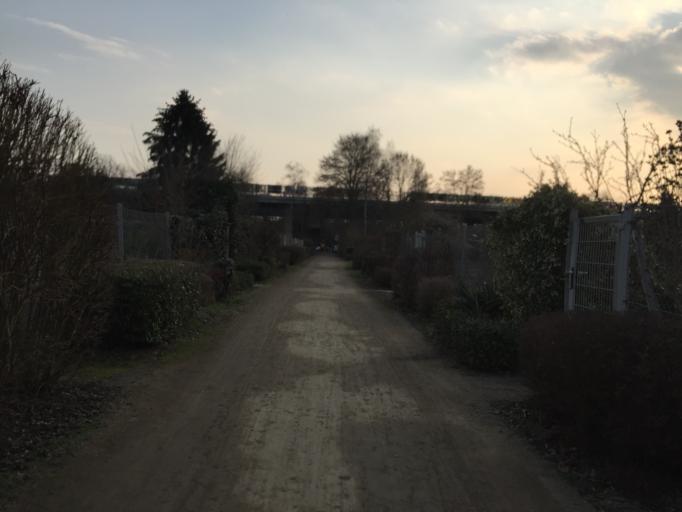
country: DE
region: Hesse
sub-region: Regierungsbezirk Darmstadt
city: Frankfurt am Main
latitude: 50.1346
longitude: 8.6405
